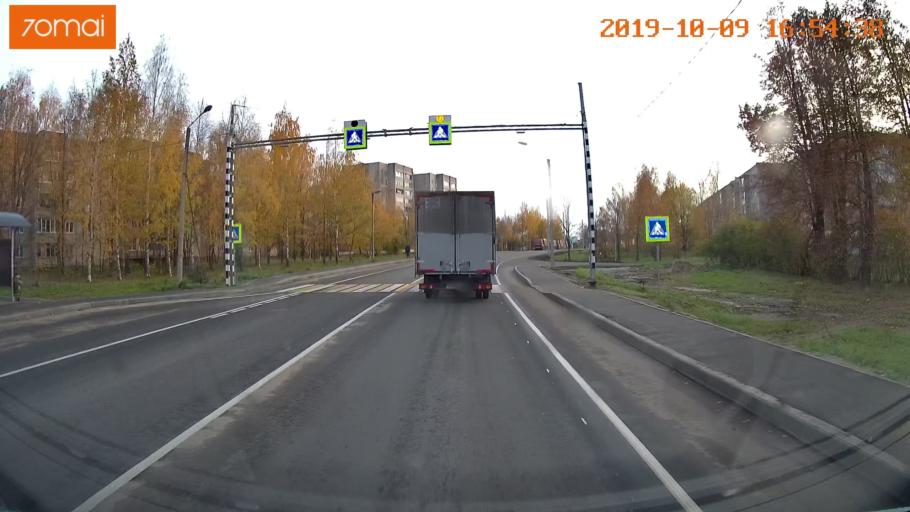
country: RU
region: Ivanovo
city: Privolzhsk
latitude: 57.3725
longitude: 41.2787
